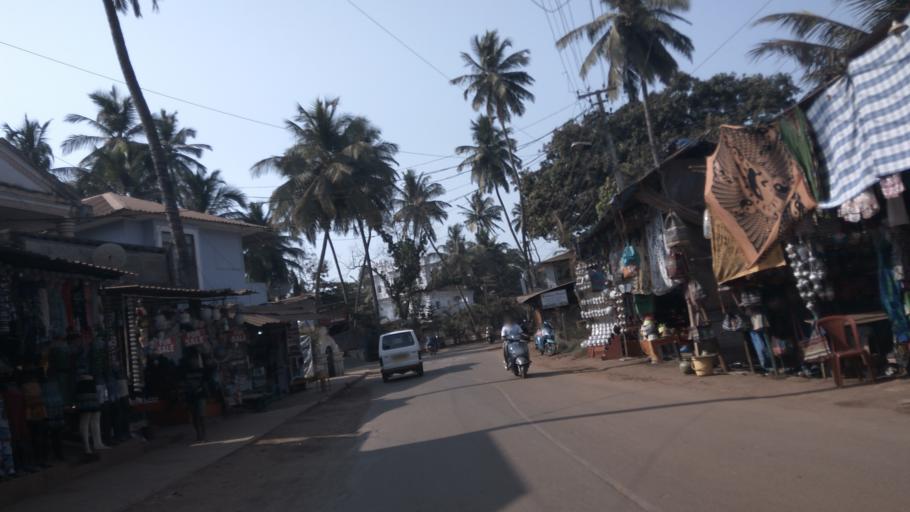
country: IN
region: Goa
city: Calangute
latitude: 15.5590
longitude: 73.7544
